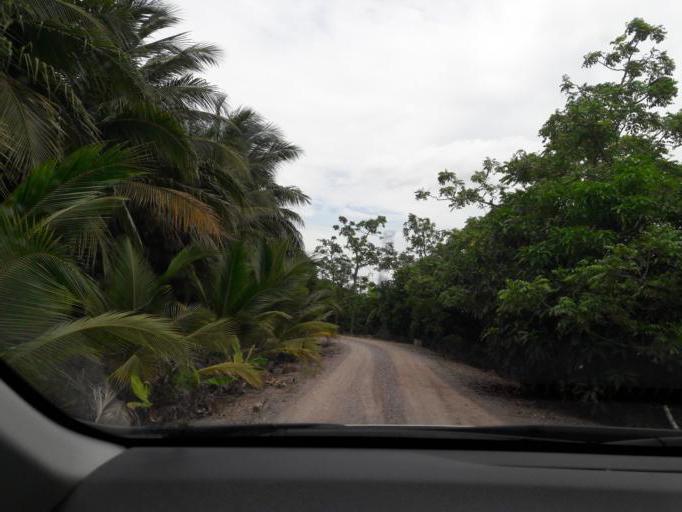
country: TH
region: Ratchaburi
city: Damnoen Saduak
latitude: 13.5546
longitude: 100.0024
